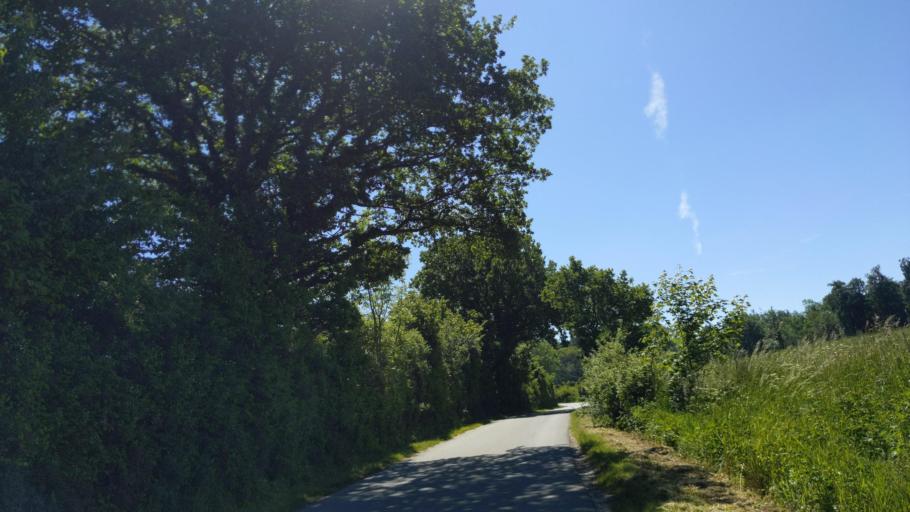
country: DE
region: Schleswig-Holstein
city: Schashagen
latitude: 54.1444
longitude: 10.8625
